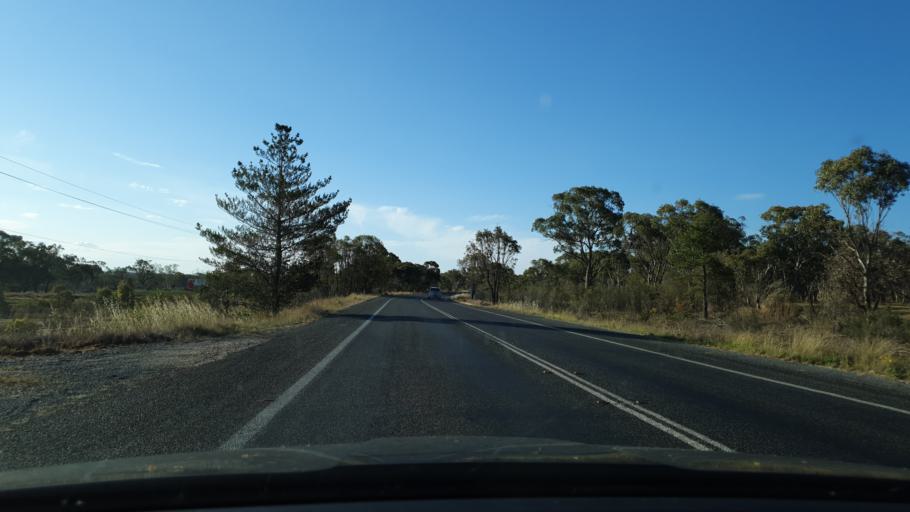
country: AU
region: Queensland
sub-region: Southern Downs
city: Stanthorpe
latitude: -28.6711
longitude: 151.9179
